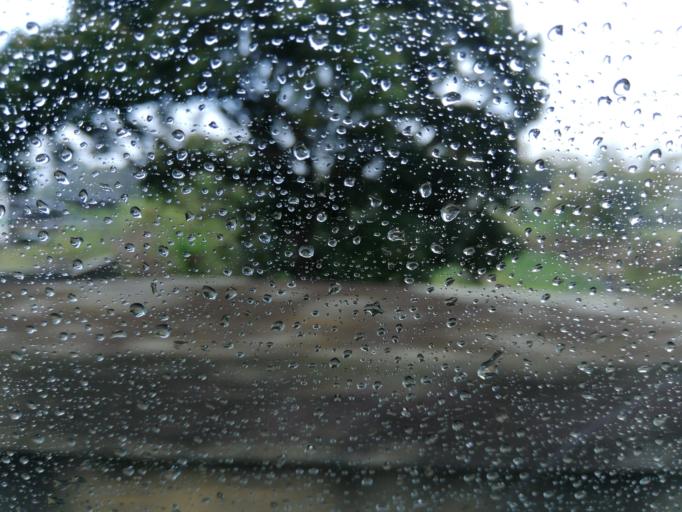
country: MU
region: Plaines Wilhems
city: Ebene
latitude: -20.2517
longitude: 57.4879
